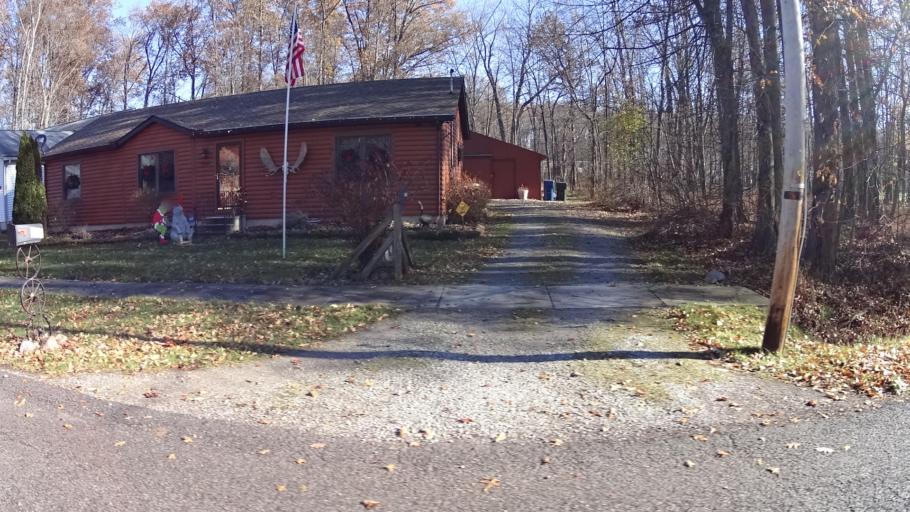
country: US
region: Ohio
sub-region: Lorain County
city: North Ridgeville
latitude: 41.4140
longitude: -81.9878
